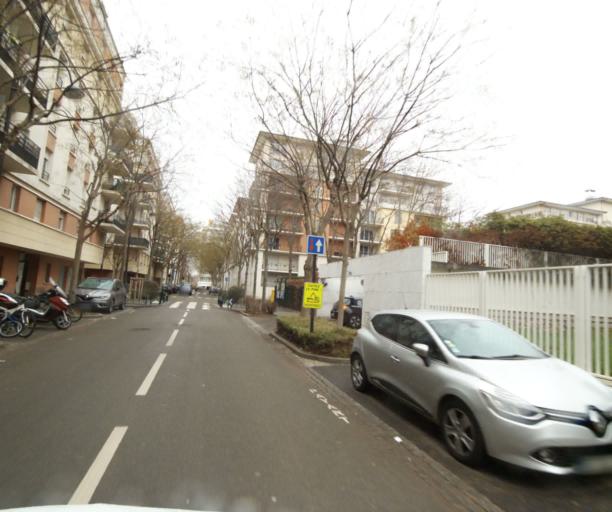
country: FR
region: Ile-de-France
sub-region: Departement des Yvelines
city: Chatou
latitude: 48.8894
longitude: 2.1737
